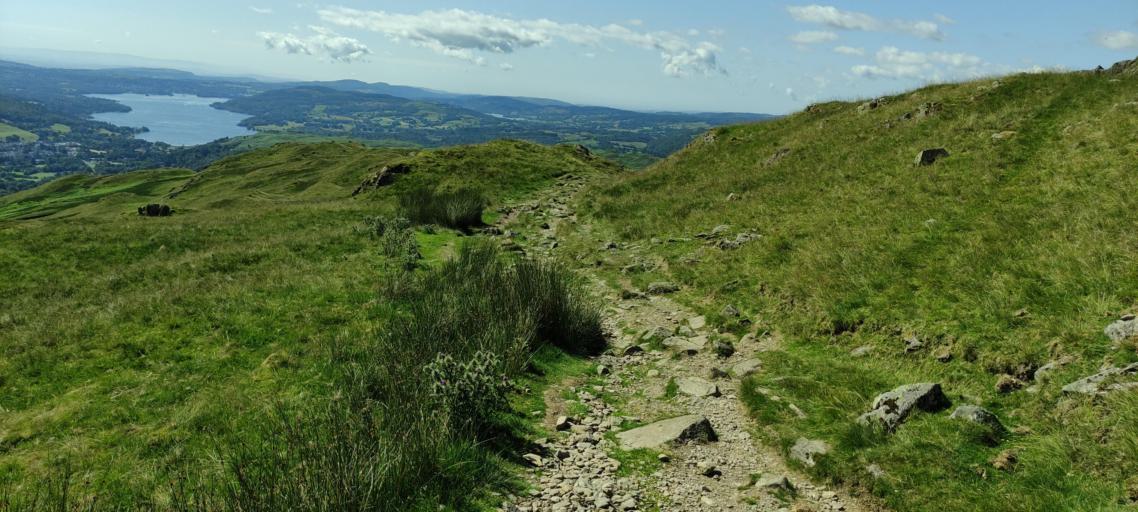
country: GB
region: England
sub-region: Cumbria
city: Ambleside
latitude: 54.4605
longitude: -2.9965
